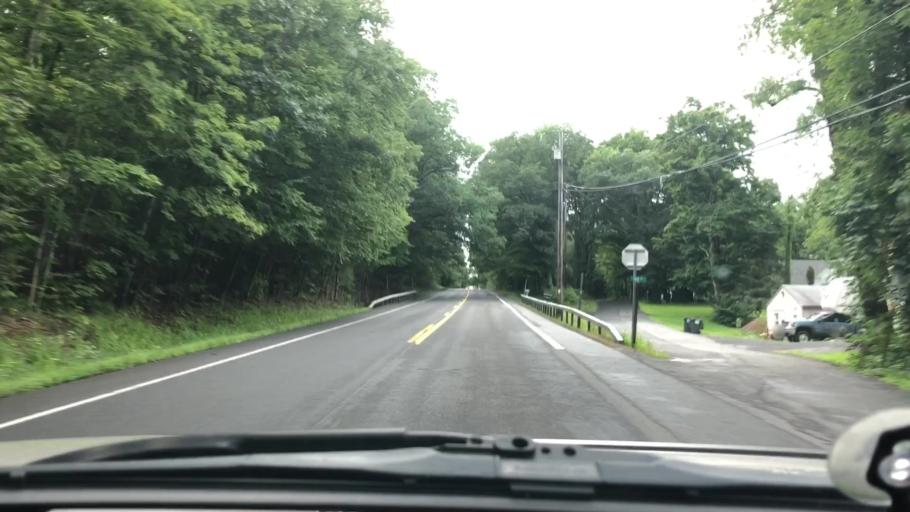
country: US
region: New York
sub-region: Greene County
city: Palenville
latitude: 42.1751
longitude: -73.9875
